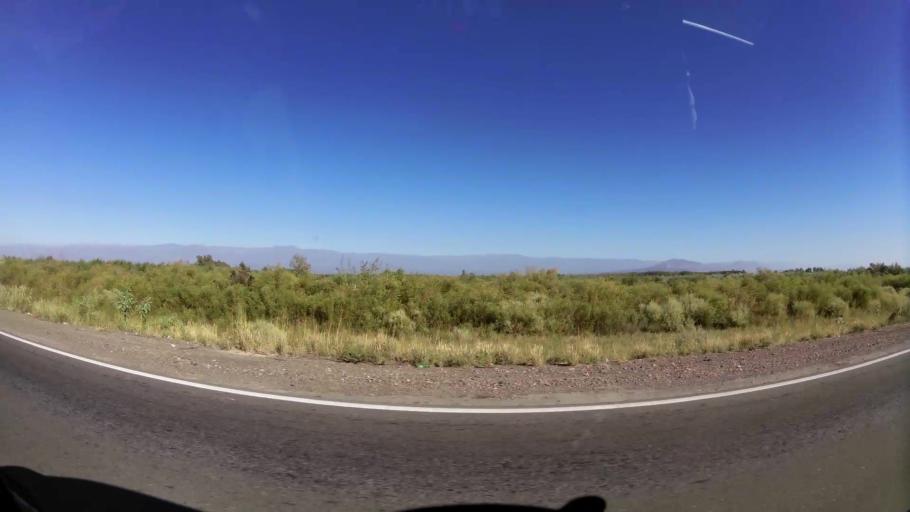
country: AR
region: Mendoza
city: General Lavalle
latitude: -32.7094
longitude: -68.6767
